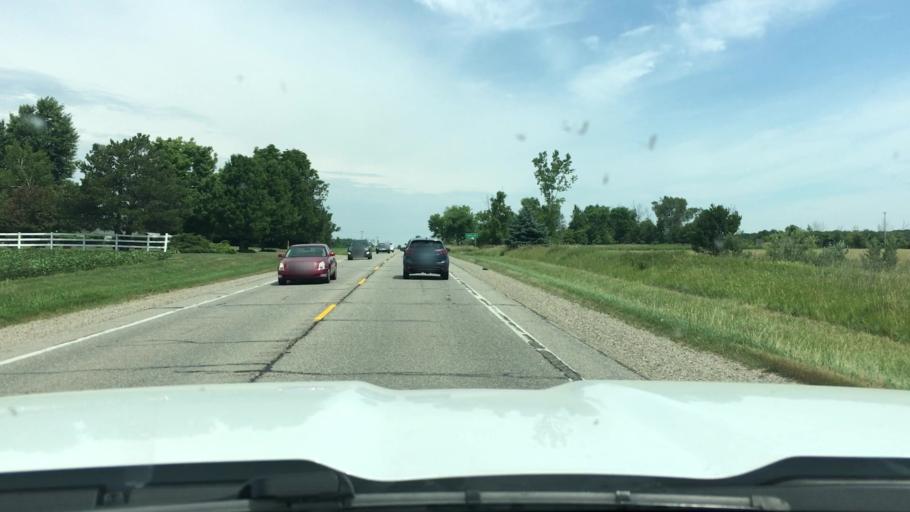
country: US
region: Michigan
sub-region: Sanilac County
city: Marlette
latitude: 43.2376
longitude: -83.0782
